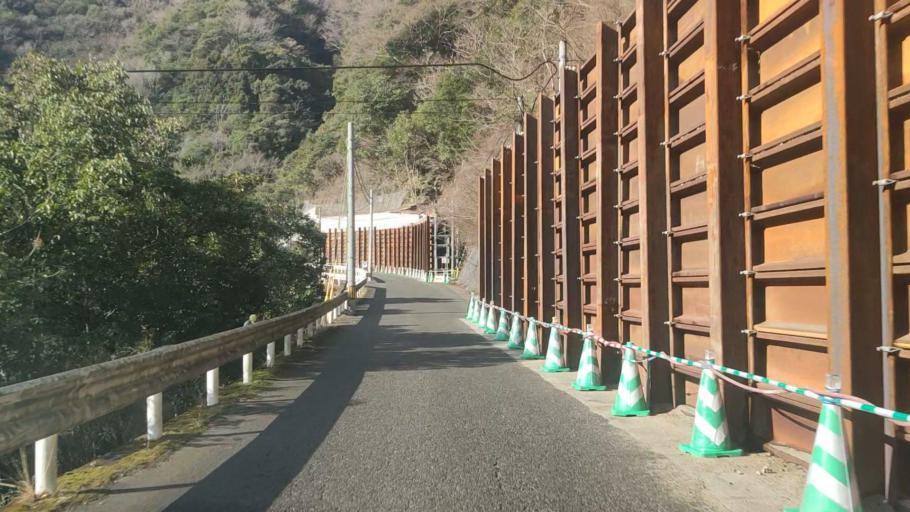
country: JP
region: Kumamoto
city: Hitoyoshi
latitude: 32.4183
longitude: 130.8473
